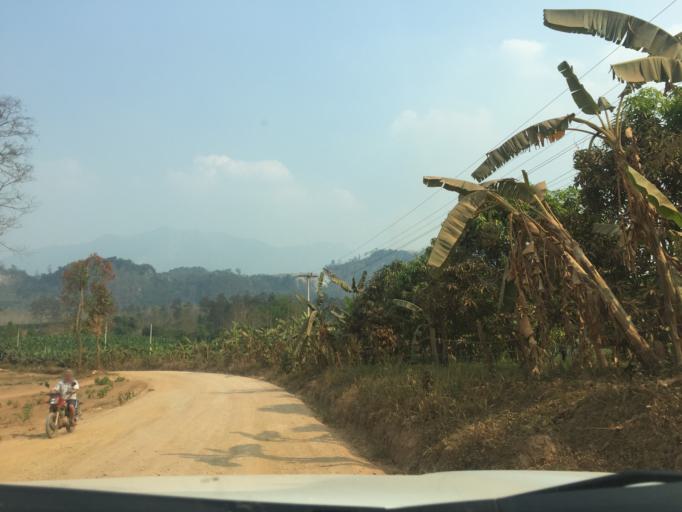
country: LA
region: Xiagnabouli
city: Sainyabuli
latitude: 19.2112
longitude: 101.6941
